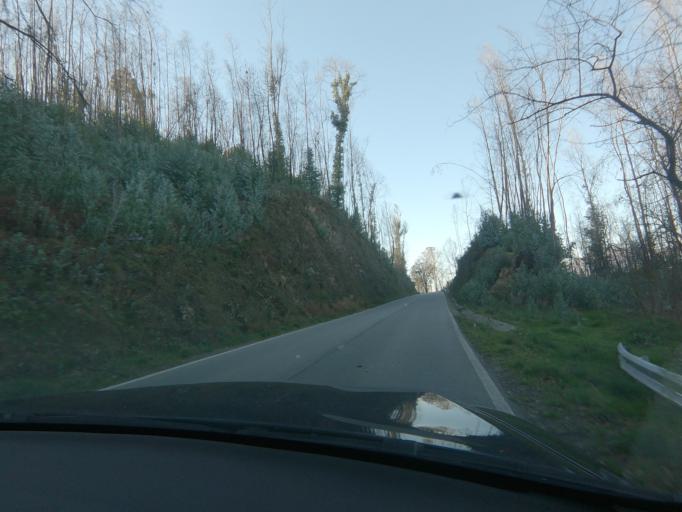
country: PT
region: Viseu
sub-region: Vouzela
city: Vouzela
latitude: 40.7295
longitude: -8.1396
